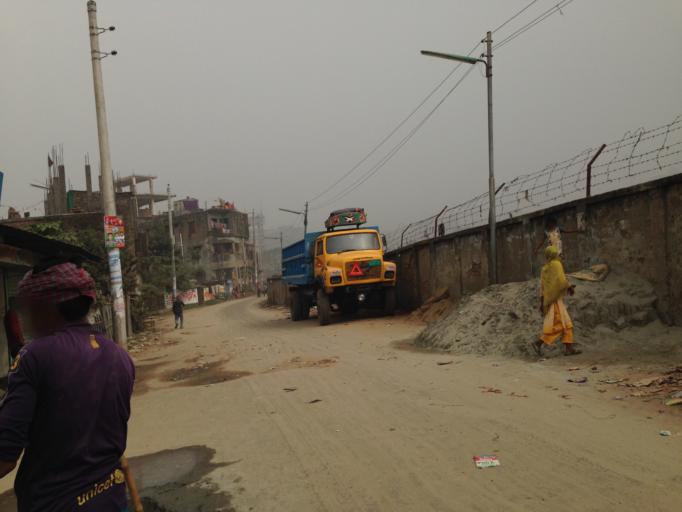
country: BD
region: Dhaka
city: Azimpur
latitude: 23.7966
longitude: 90.3431
